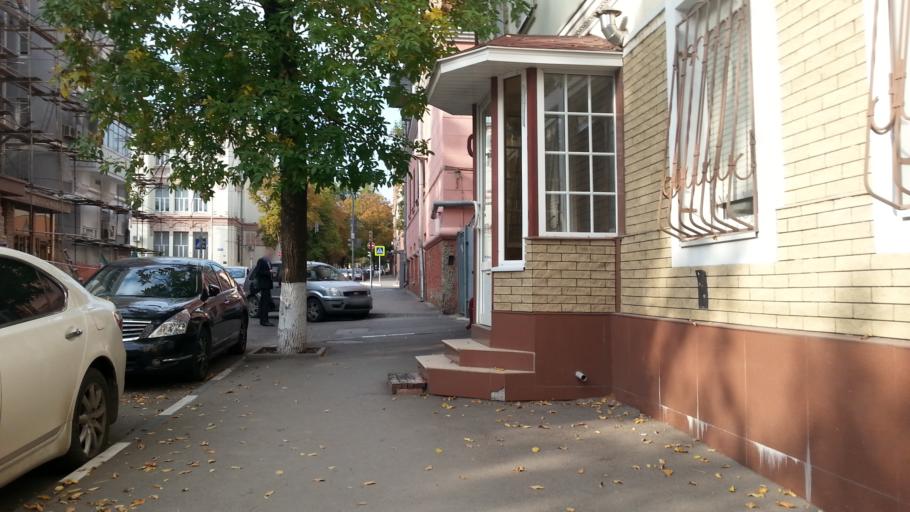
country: RU
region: Rostov
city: Rostov-na-Donu
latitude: 47.2248
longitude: 39.7088
